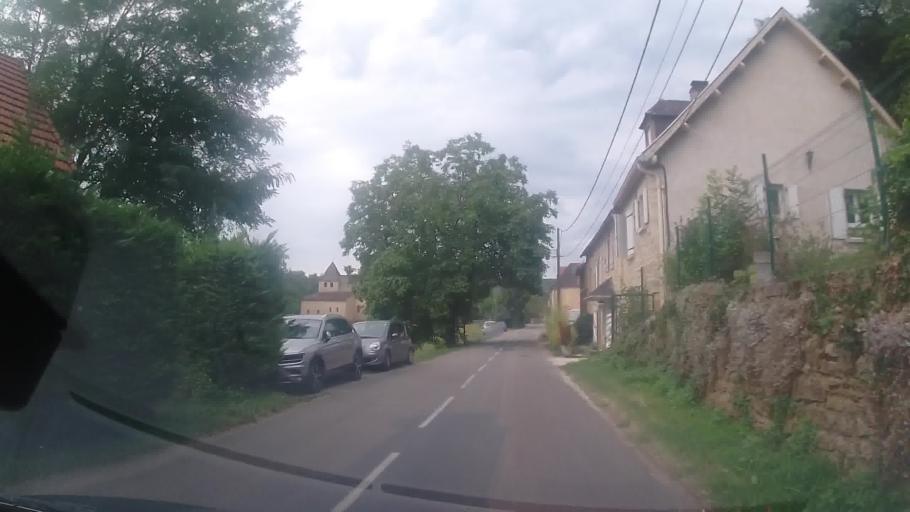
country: FR
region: Aquitaine
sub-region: Departement de la Dordogne
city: Carsac-Aillac
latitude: 44.8423
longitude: 1.2711
